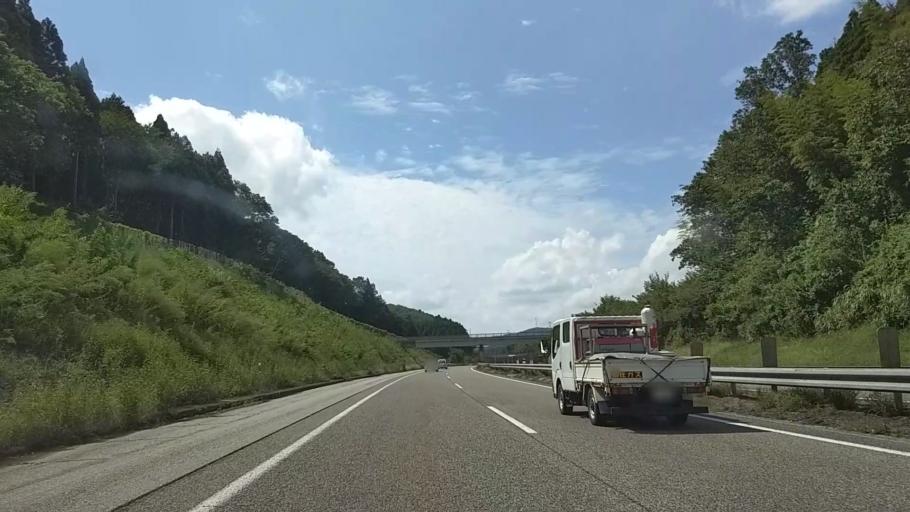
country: JP
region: Toyama
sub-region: Oyabe Shi
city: Oyabe
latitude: 36.6256
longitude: 136.8354
